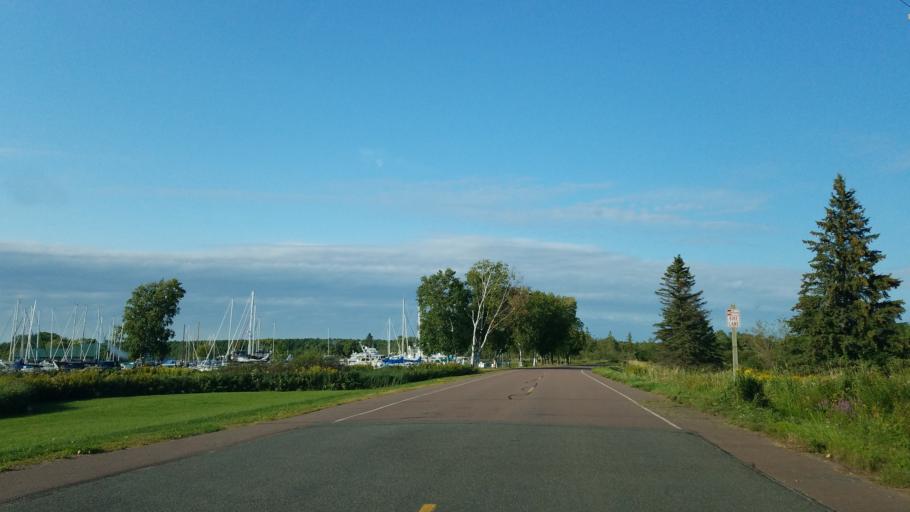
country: US
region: Wisconsin
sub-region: Bayfield County
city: Washburn
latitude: 46.7702
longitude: -90.7805
